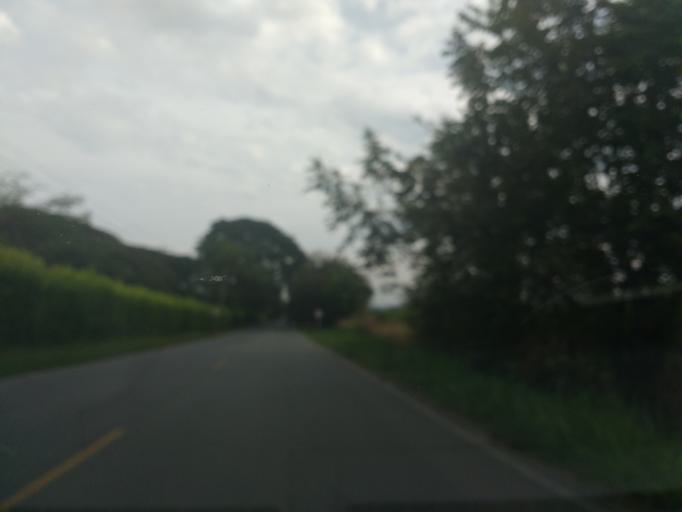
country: CO
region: Valle del Cauca
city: Florida
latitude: 3.3050
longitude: -76.2333
